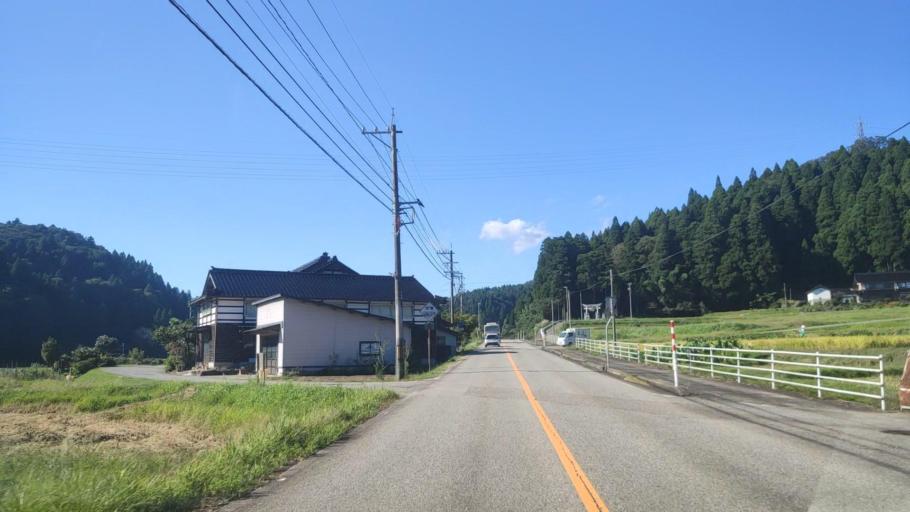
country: JP
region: Ishikawa
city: Nanao
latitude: 37.2729
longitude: 137.0555
